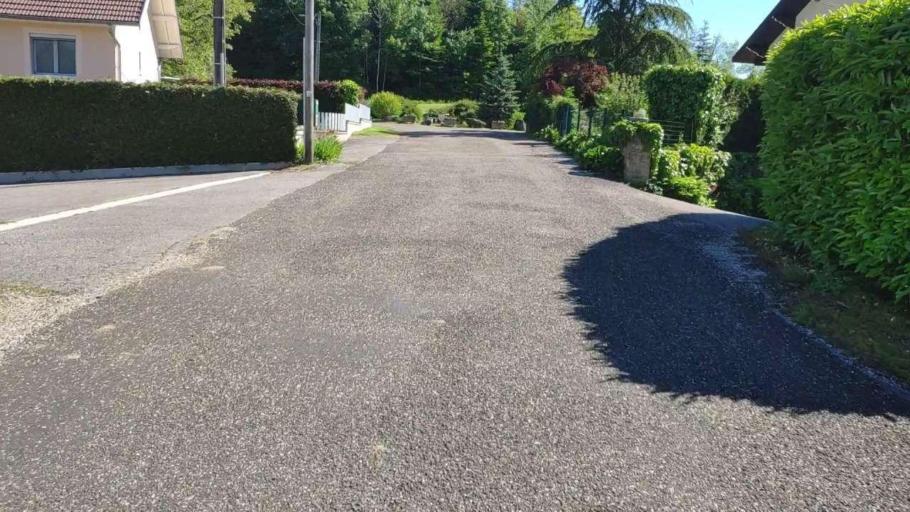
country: FR
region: Franche-Comte
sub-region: Departement du Jura
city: Perrigny
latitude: 46.7159
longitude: 5.5774
